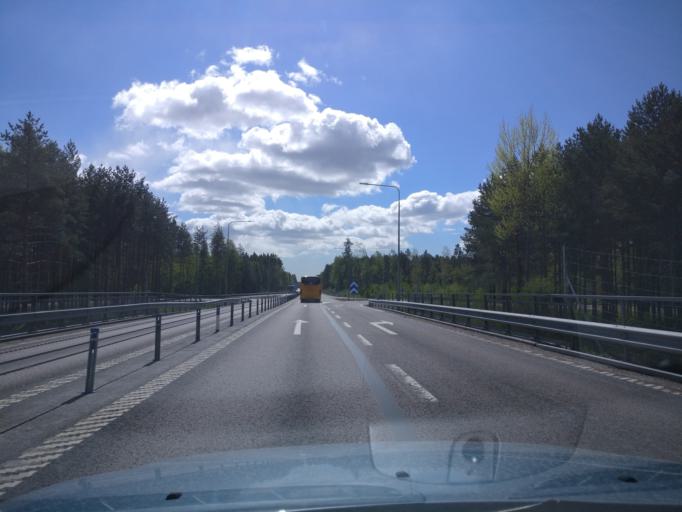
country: SE
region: Vaermland
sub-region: Karlstads Kommun
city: Karlstad
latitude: 59.4189
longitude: 13.5328
